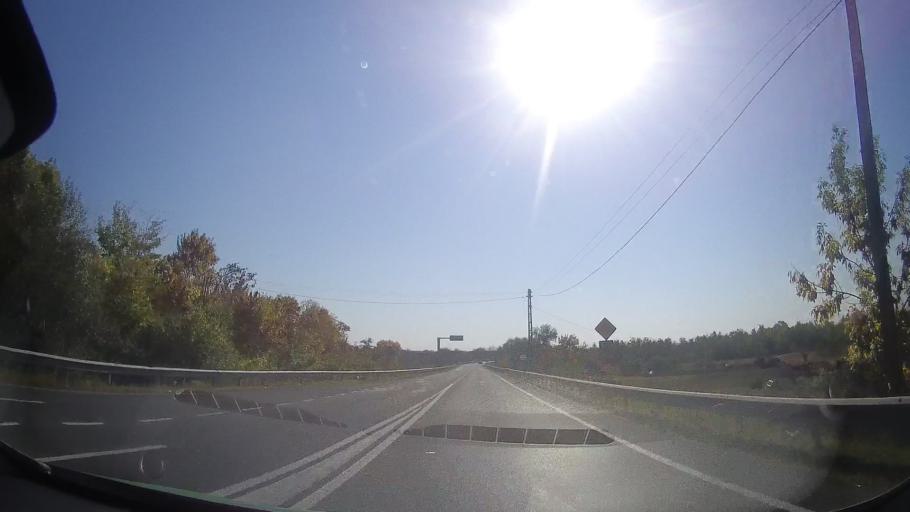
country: RO
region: Timis
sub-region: Comuna Belint
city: Belint
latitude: 45.7624
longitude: 21.7272
